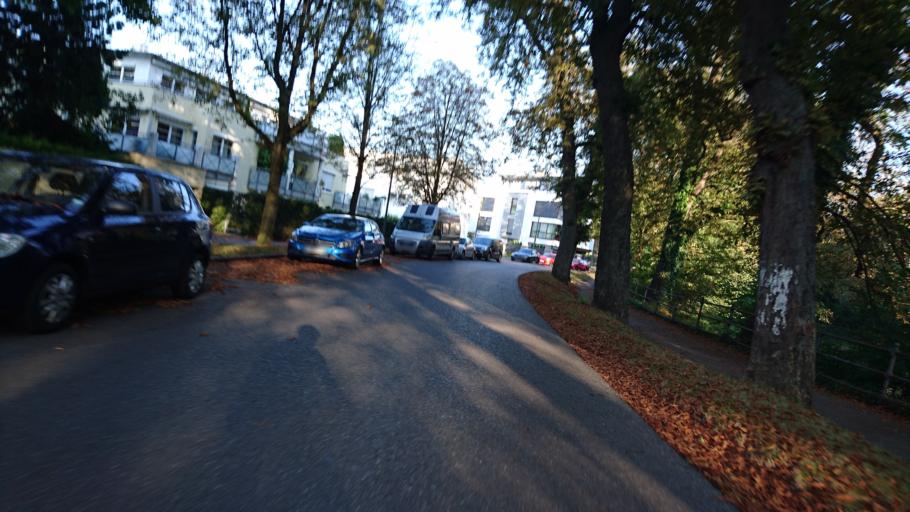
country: DE
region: Bavaria
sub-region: Swabia
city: Augsburg
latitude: 48.3762
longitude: 10.9065
